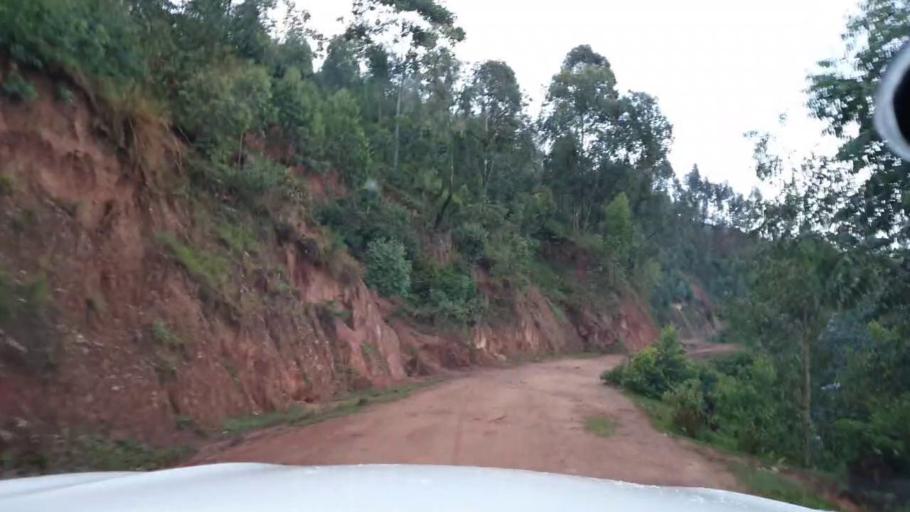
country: BI
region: Kayanza
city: Kayanza
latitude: -2.7187
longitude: 29.5440
